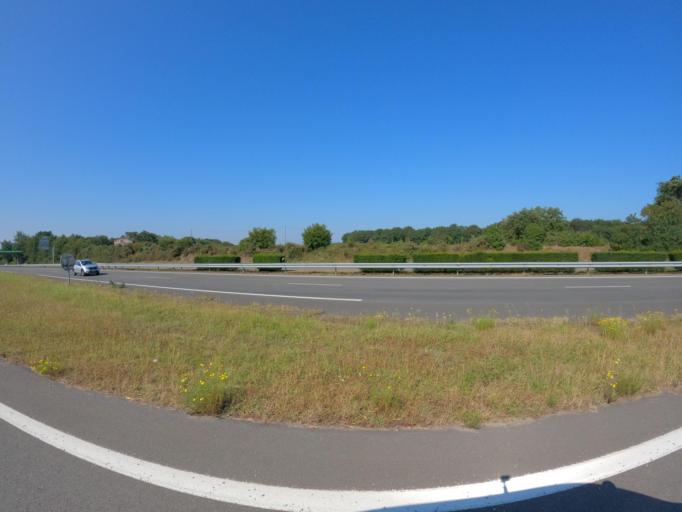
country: FR
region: Pays de la Loire
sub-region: Departement de la Loire-Atlantique
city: La Chevroliere
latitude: 47.0808
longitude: -1.5648
